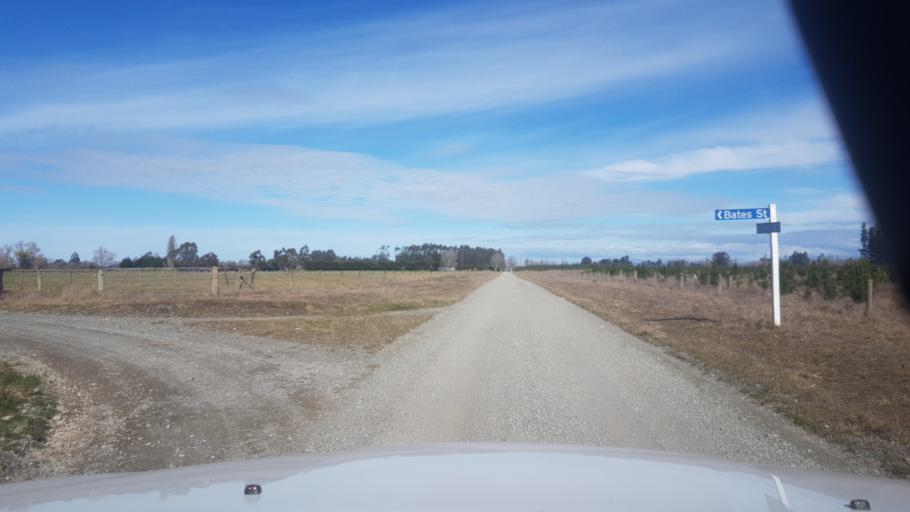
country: NZ
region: Canterbury
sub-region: Timaru District
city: Pleasant Point
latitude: -44.1314
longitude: 171.2795
